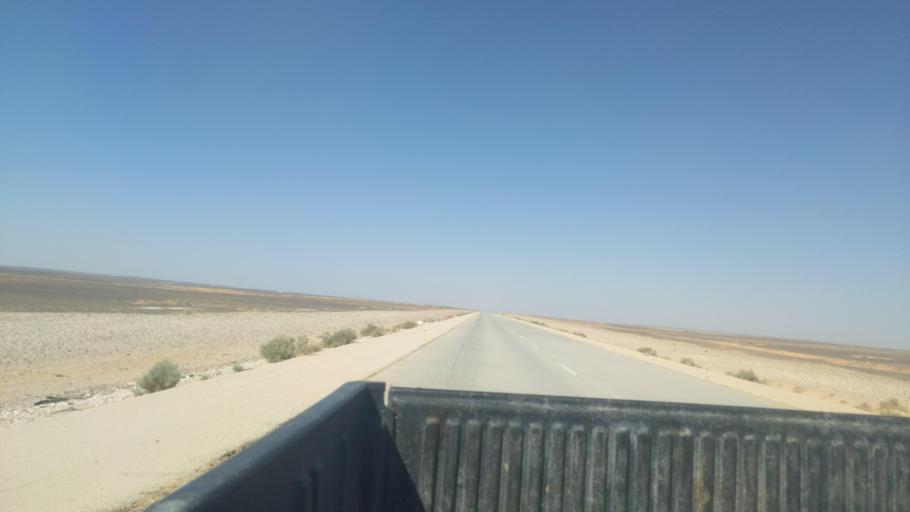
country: JO
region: Amman
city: Al Azraq ash Shamali
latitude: 31.4570
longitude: 36.7864
